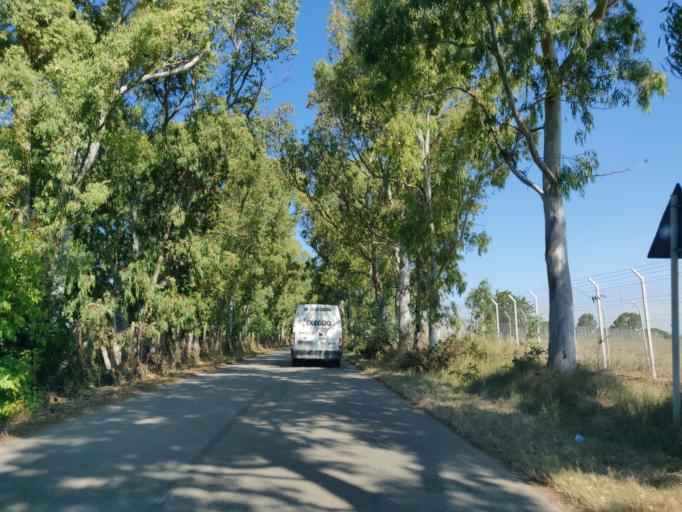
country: IT
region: Latium
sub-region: Citta metropolitana di Roma Capitale
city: Aurelia
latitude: 42.1641
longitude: 11.7436
